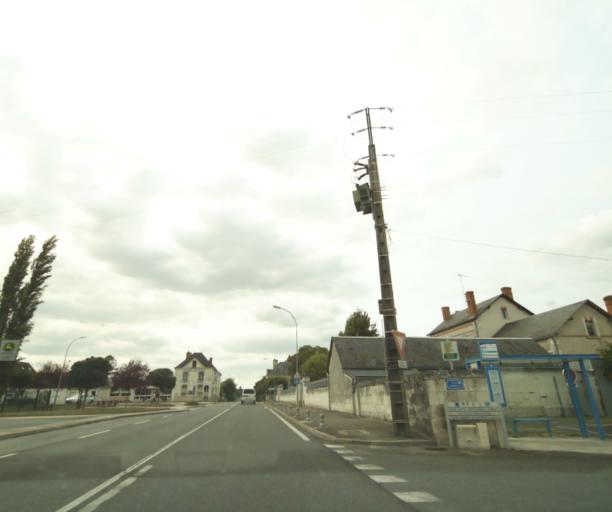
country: FR
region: Centre
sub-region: Departement d'Indre-et-Loire
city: Perrusson
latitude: 47.0825
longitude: 1.0359
